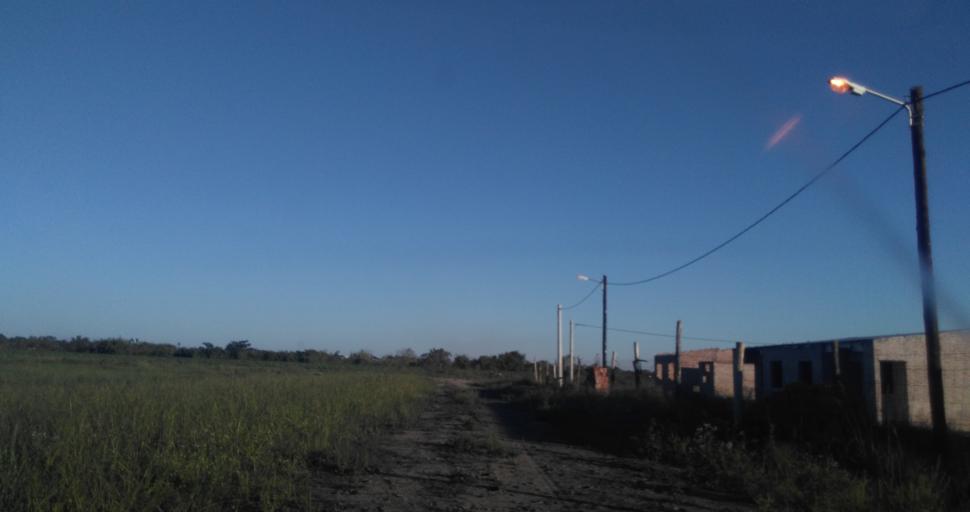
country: AR
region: Chaco
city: Fontana
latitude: -27.3958
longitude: -58.9854
